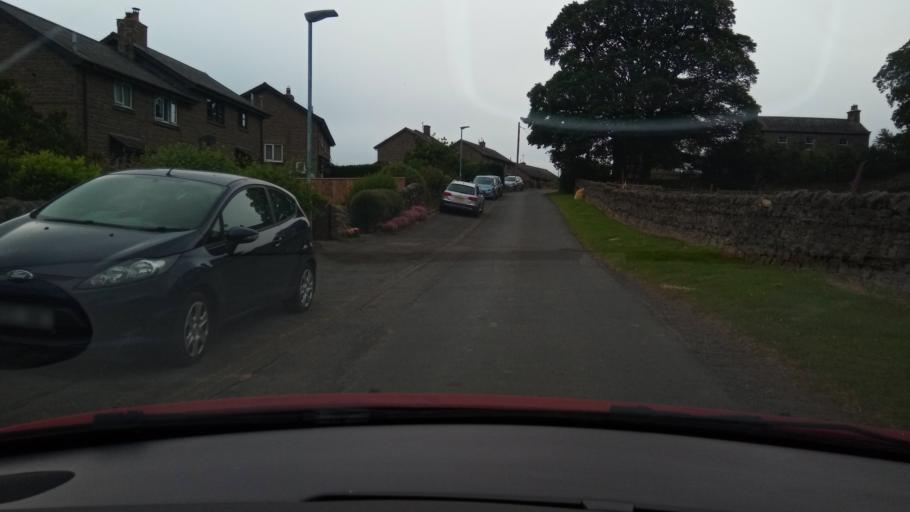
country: GB
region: England
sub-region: Northumberland
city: Rochester
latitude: 55.2765
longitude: -2.2645
